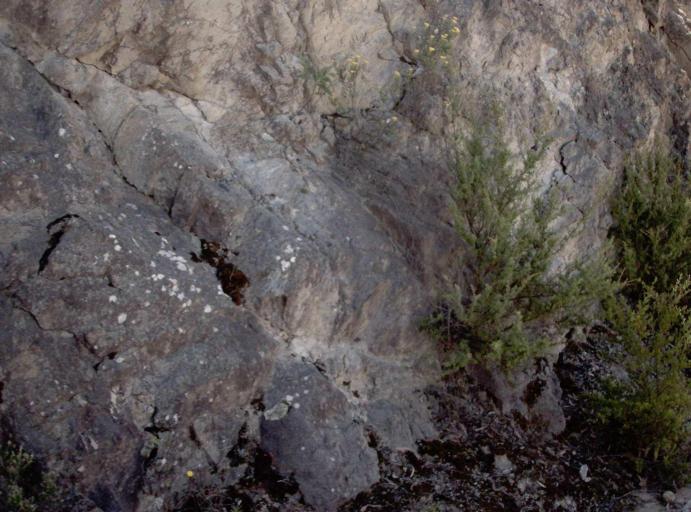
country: AU
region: New South Wales
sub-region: Snowy River
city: Jindabyne
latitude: -37.0882
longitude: 148.3302
